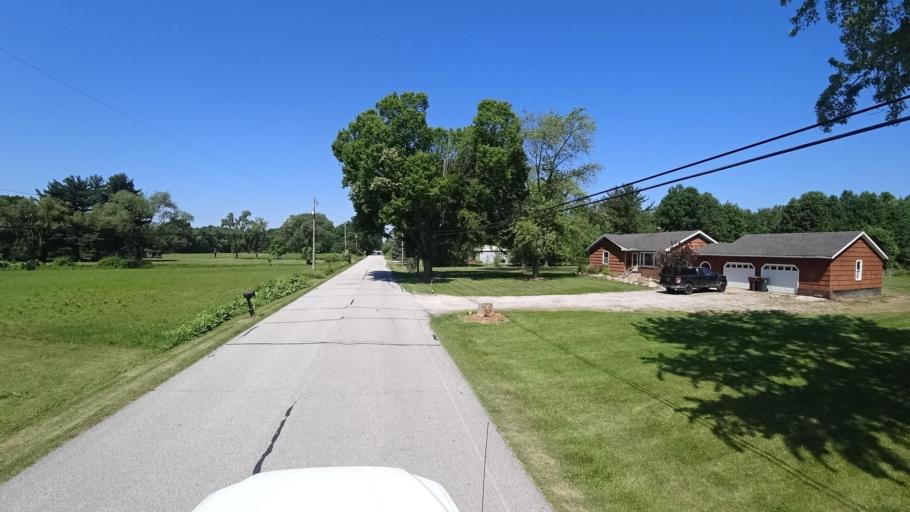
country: US
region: Indiana
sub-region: Porter County
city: Burns Harbor
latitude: 41.6104
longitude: -87.1189
